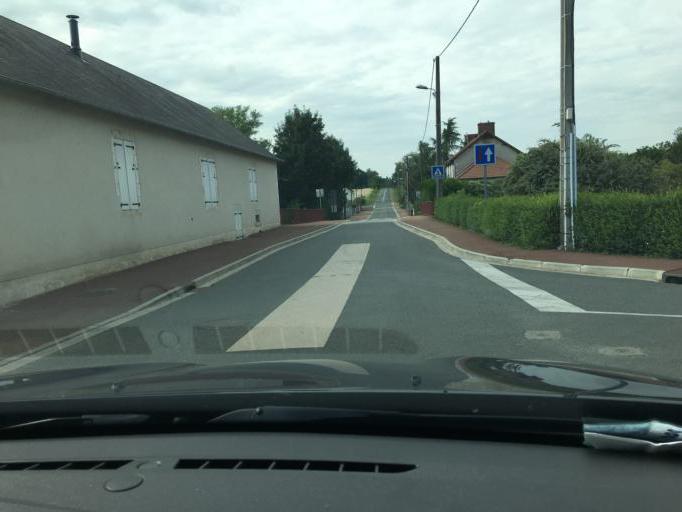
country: FR
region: Centre
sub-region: Departement du Cher
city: Rians
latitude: 47.2008
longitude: 2.5713
